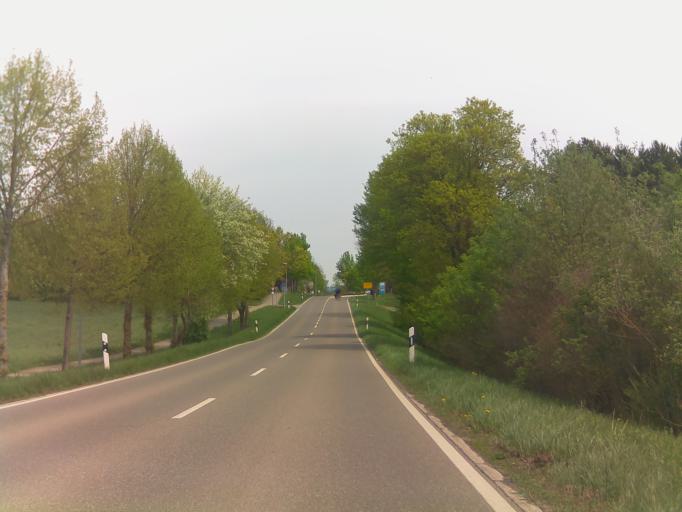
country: DE
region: Baden-Wuerttemberg
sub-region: Freiburg Region
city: Deisslingen
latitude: 48.1217
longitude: 8.6173
